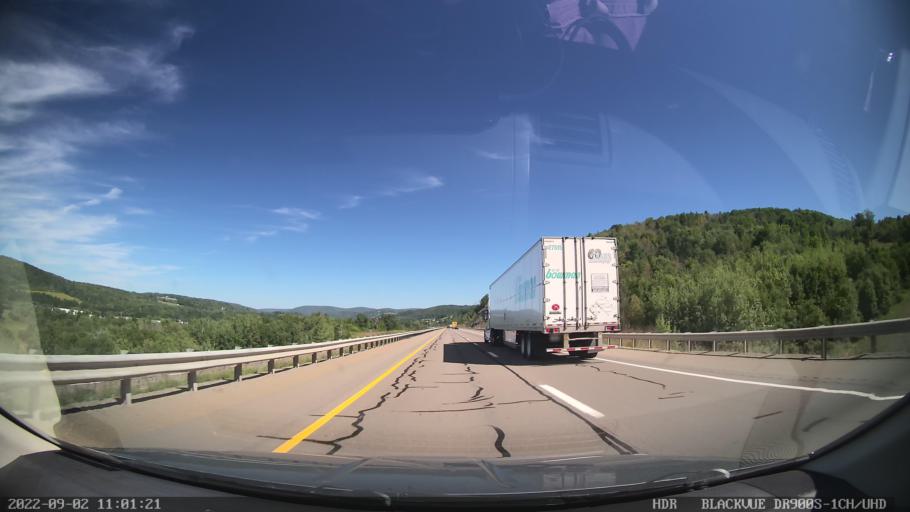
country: US
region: Pennsylvania
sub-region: Tioga County
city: Mansfield
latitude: 41.7592
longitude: -77.0695
